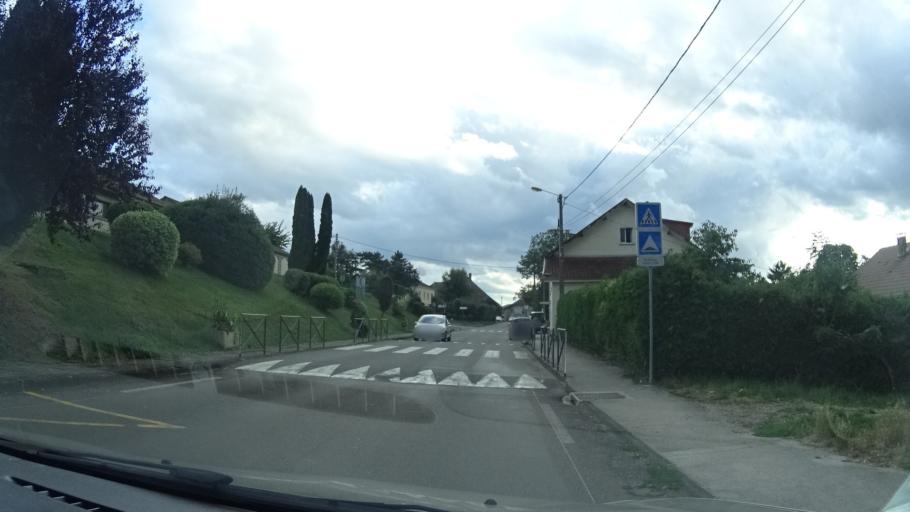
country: FR
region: Franche-Comte
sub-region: Departement du Doubs
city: Saone
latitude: 47.2221
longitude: 6.1145
